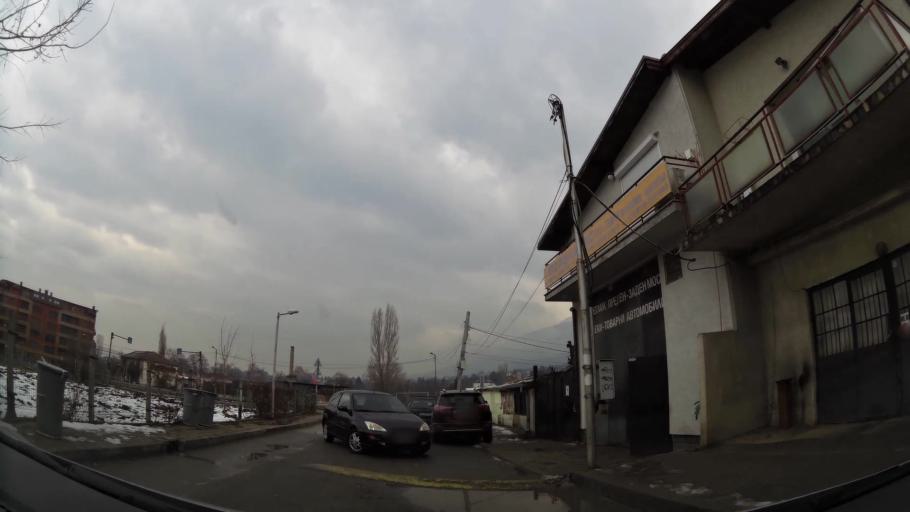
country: BG
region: Sofia-Capital
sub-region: Stolichna Obshtina
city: Sofia
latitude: 42.6636
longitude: 23.2455
